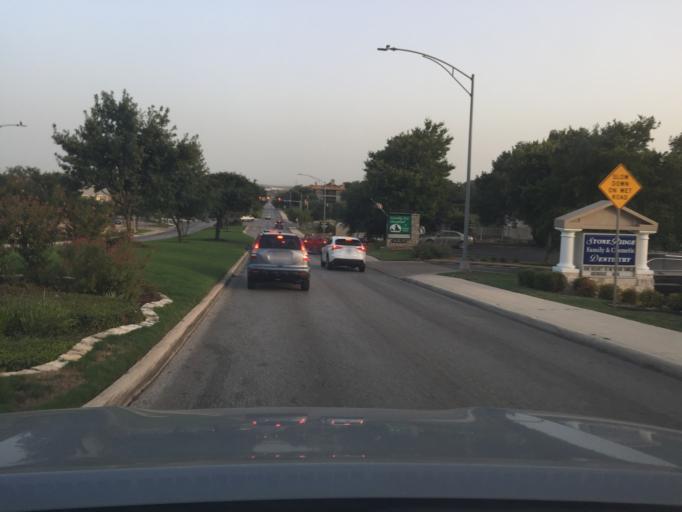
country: US
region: Texas
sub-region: Bexar County
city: Hollywood Park
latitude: 29.6342
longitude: -98.4958
